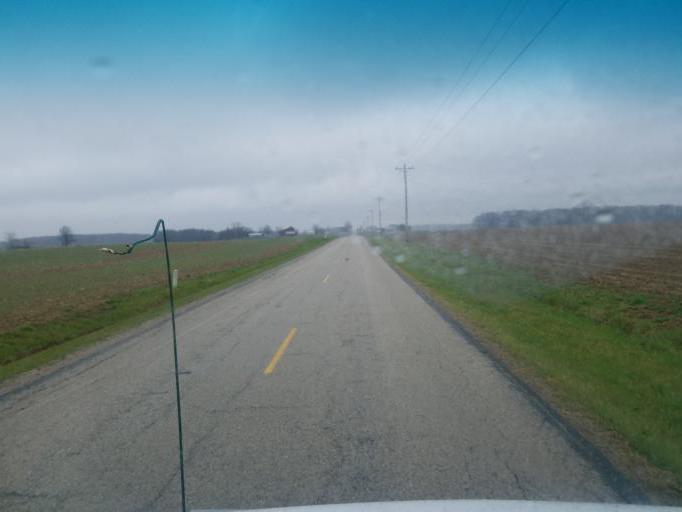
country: US
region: Ohio
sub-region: Crawford County
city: Bucyrus
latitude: 40.9650
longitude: -82.9747
